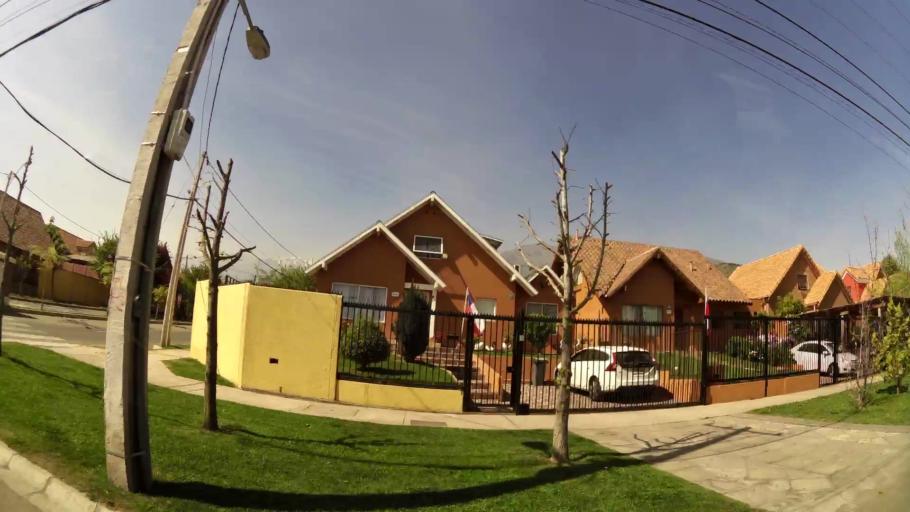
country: CL
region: Santiago Metropolitan
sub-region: Provincia de Cordillera
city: Puente Alto
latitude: -33.5385
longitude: -70.5511
